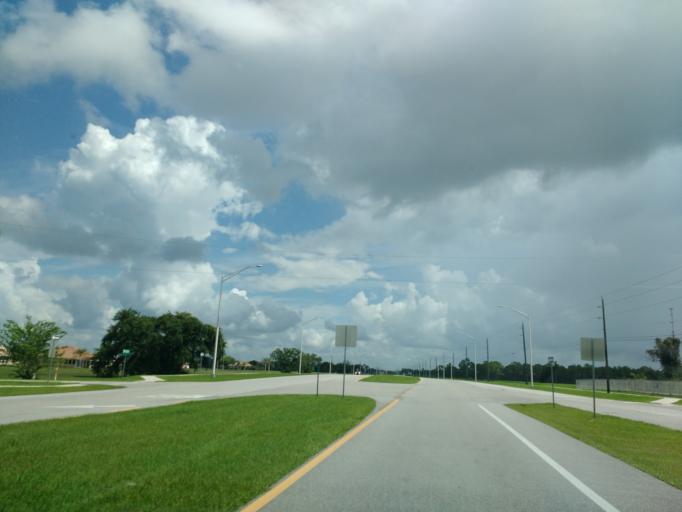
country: US
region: Florida
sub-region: Lee County
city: Burnt Store Marina
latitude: 26.7726
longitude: -82.0381
